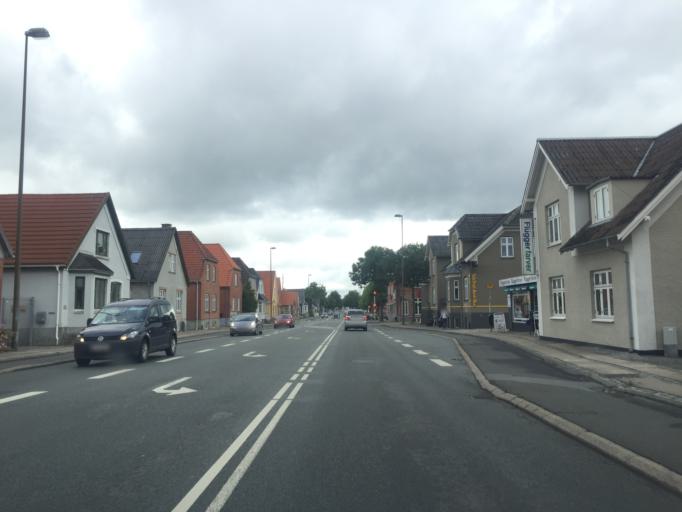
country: DK
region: South Denmark
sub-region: Odense Kommune
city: Odense
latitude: 55.3693
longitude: 10.3719
